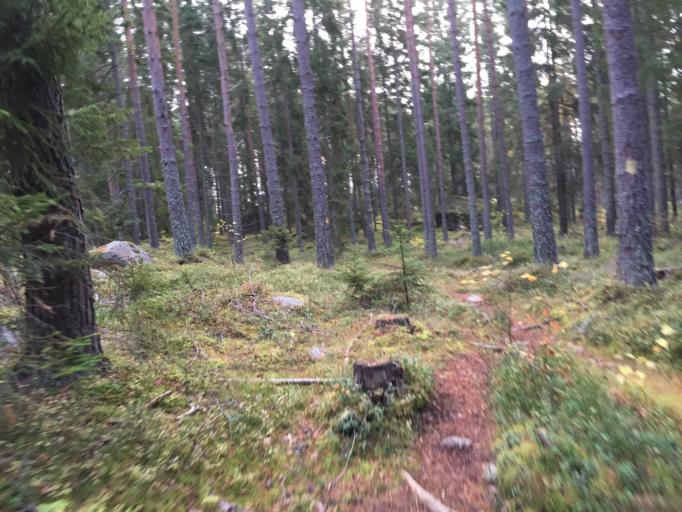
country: SE
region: Vaestmanland
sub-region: Hallstahammars Kommun
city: Hallstahammar
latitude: 59.6340
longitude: 16.2483
